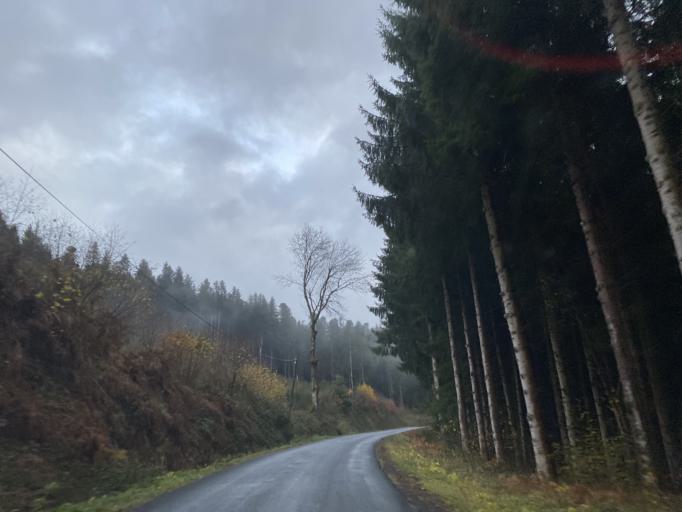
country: FR
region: Auvergne
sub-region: Departement du Puy-de-Dome
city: Cunlhat
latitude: 45.5866
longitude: 3.5622
